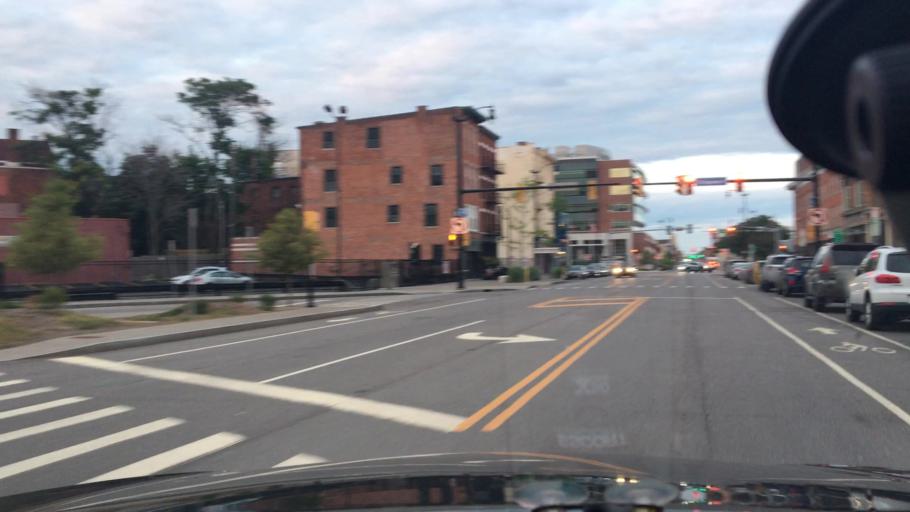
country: US
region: New York
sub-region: Erie County
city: Buffalo
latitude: 42.8894
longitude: -78.8707
